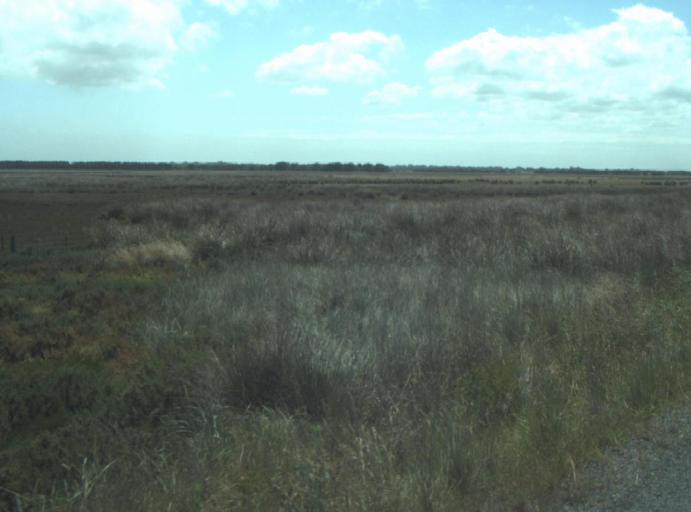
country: AU
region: Victoria
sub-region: Greater Geelong
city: Breakwater
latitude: -38.2916
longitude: 144.3792
